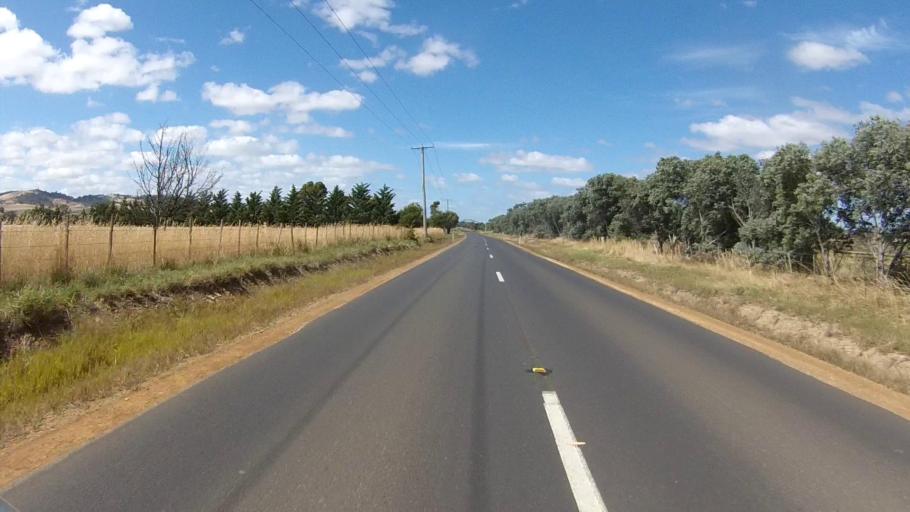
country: AU
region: Tasmania
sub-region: Clarence
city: Cambridge
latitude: -42.7144
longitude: 147.4310
